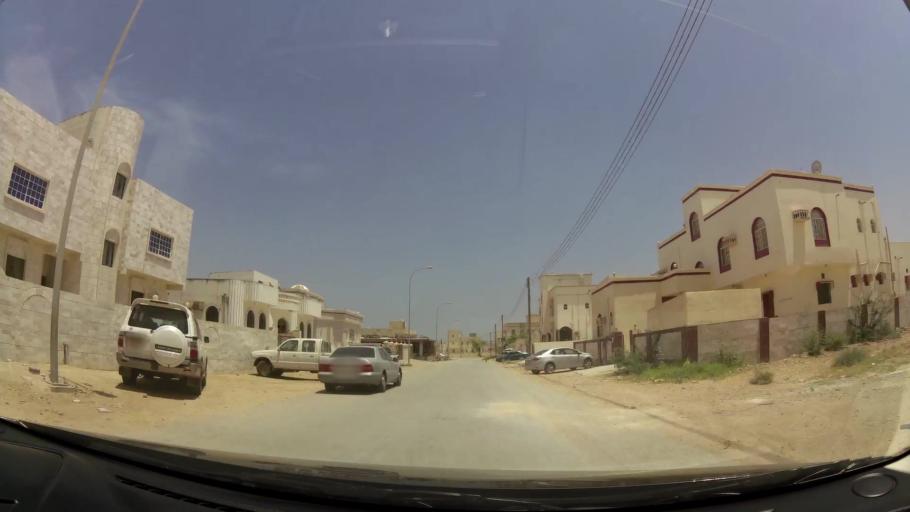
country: OM
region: Zufar
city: Salalah
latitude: 17.0713
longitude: 54.1487
